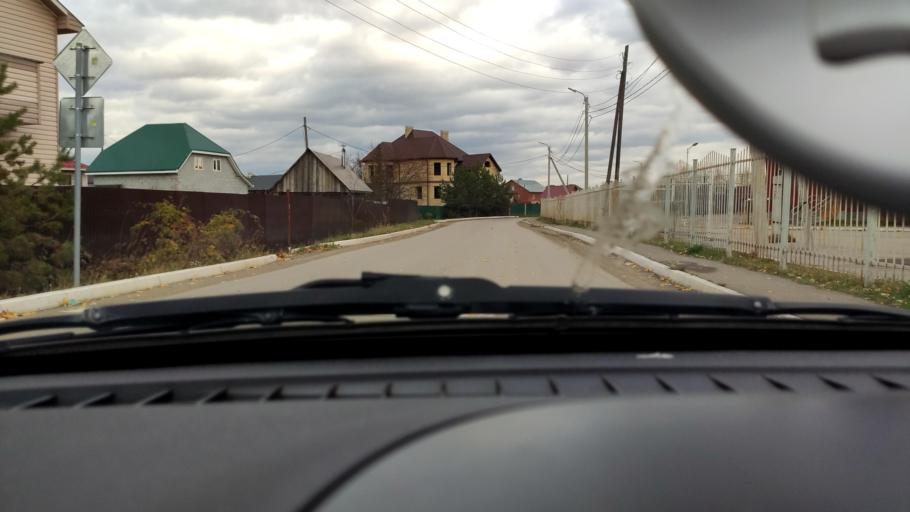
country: RU
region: Perm
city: Kondratovo
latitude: 57.9782
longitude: 56.0994
